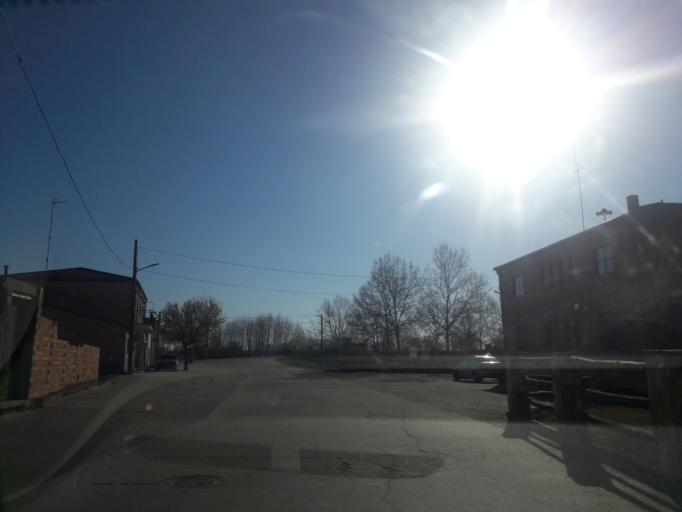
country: ES
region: Castille and Leon
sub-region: Provincia de Salamanca
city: Penarandilla
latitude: 40.8820
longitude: -5.3933
